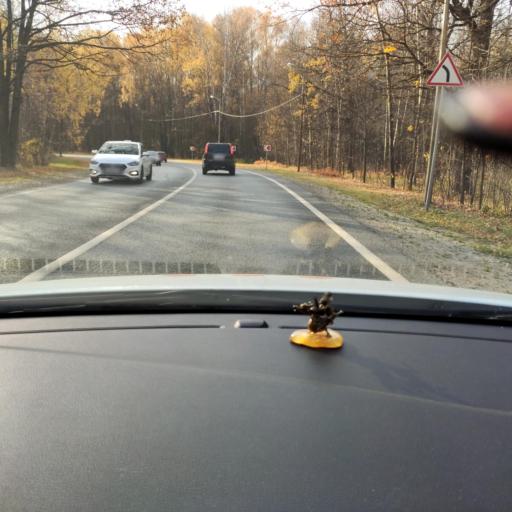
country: RU
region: Tatarstan
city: Osinovo
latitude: 55.8416
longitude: 48.8913
